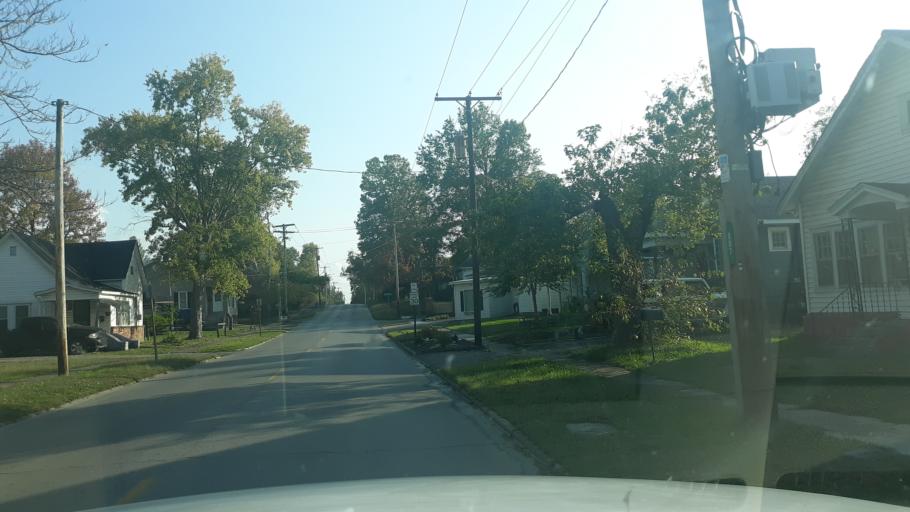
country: US
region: Illinois
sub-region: Saline County
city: Harrisburg
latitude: 37.7291
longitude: -88.5403
